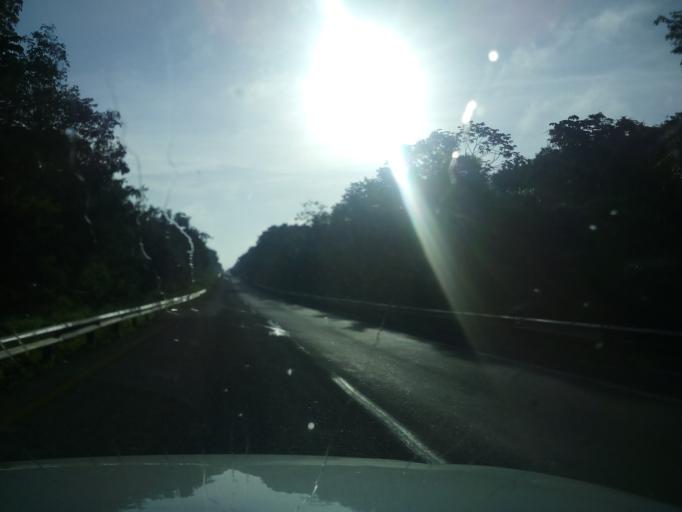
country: MX
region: Yucatan
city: Piste
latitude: 20.7433
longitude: -88.6777
